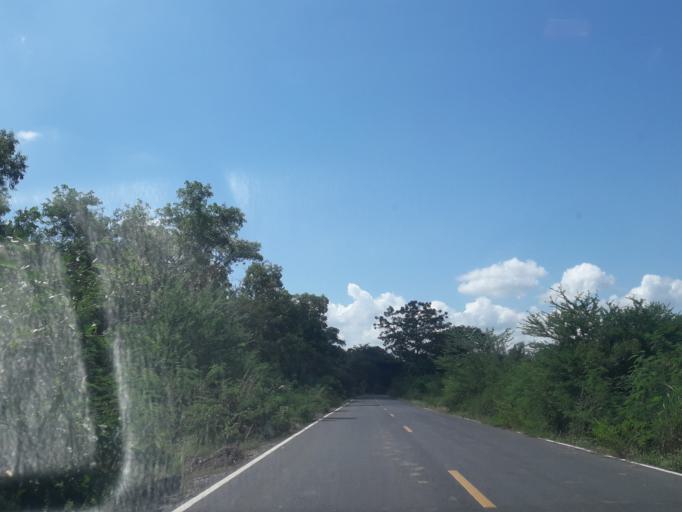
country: TH
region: Lop Buri
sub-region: Amphoe Tha Luang
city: Tha Luang
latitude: 15.0547
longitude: 101.0318
